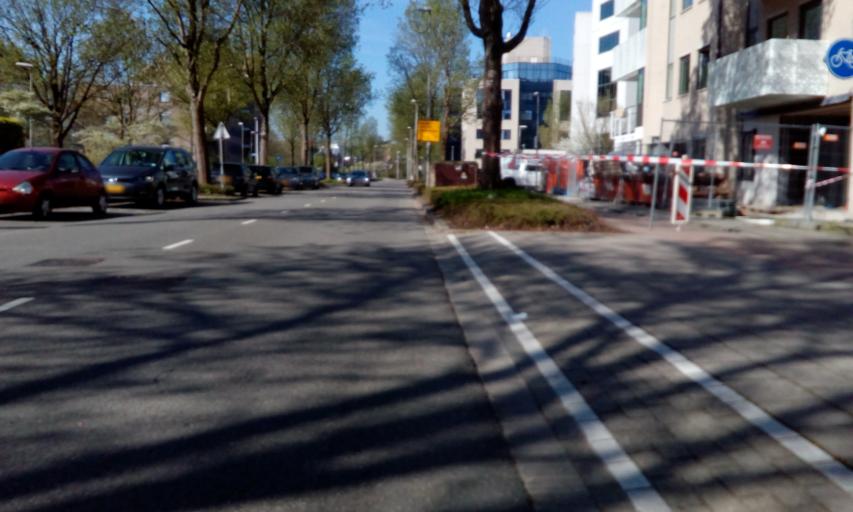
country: NL
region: South Holland
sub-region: Gemeente Zoetermeer
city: Zoetermeer
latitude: 52.0604
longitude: 4.4923
